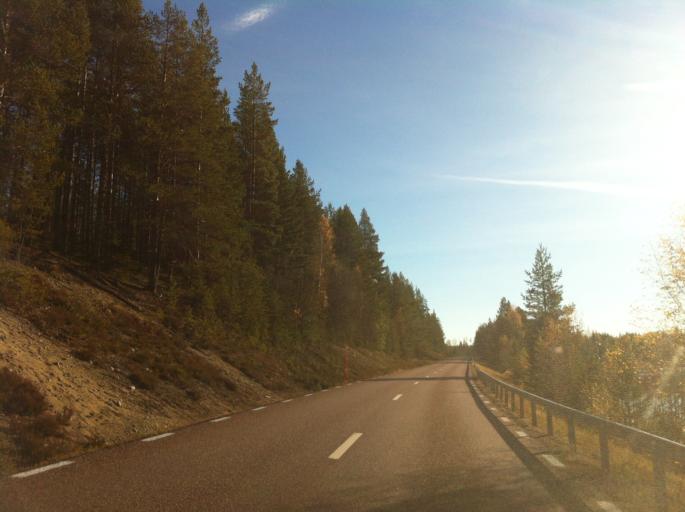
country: NO
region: Hedmark
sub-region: Trysil
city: Innbygda
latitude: 61.8234
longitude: 12.8860
